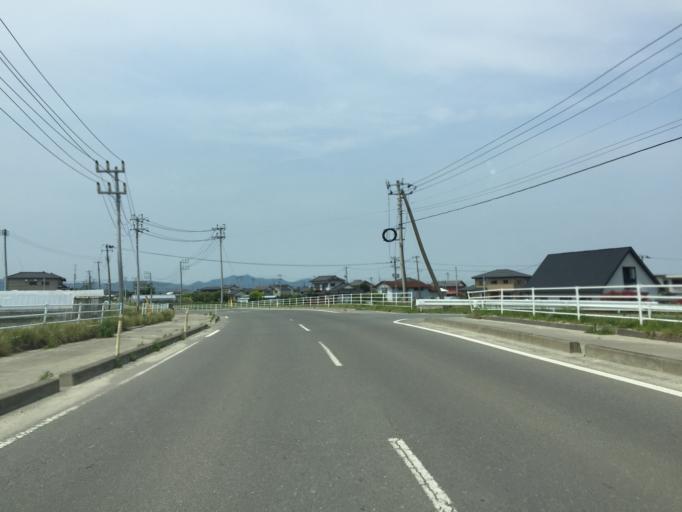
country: JP
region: Miyagi
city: Marumori
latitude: 37.7838
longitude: 140.9629
